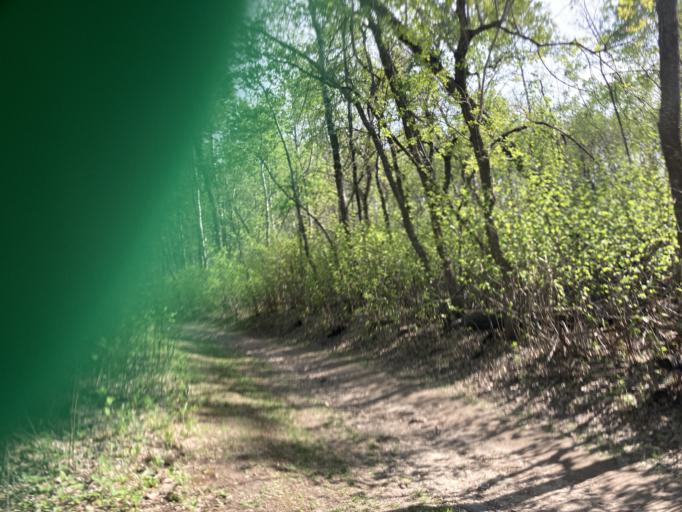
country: CA
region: Manitoba
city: Brandon
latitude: 49.7195
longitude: -99.9060
